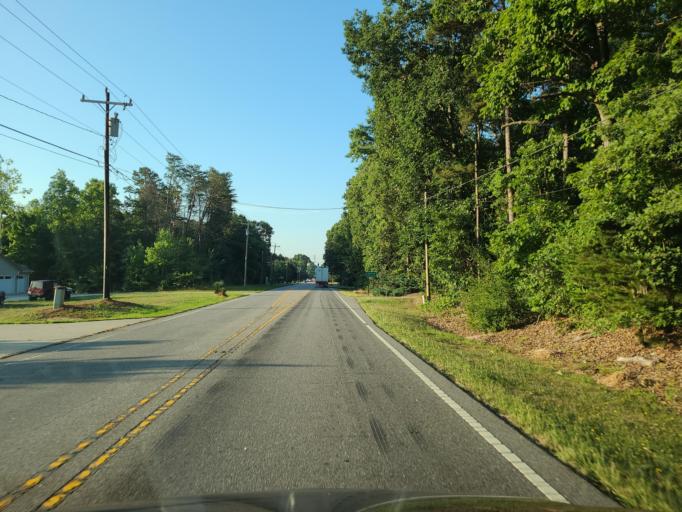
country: US
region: North Carolina
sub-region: Catawba County
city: Mountain View
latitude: 35.6654
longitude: -81.3821
